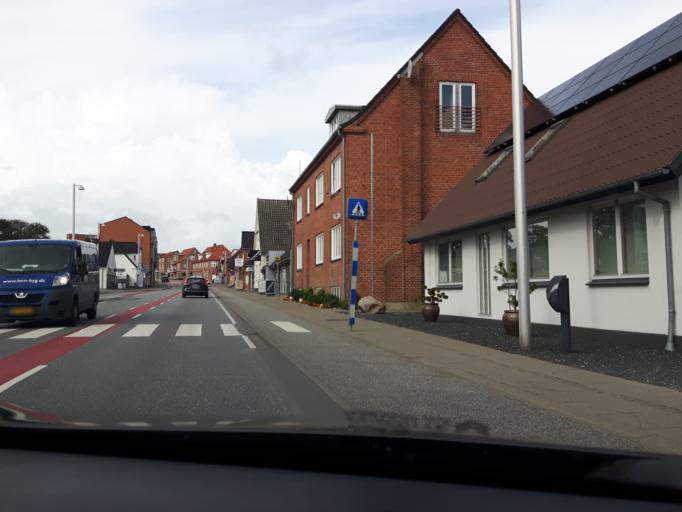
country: DK
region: North Denmark
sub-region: Jammerbugt Kommune
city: Brovst
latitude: 57.0974
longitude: 9.5266
